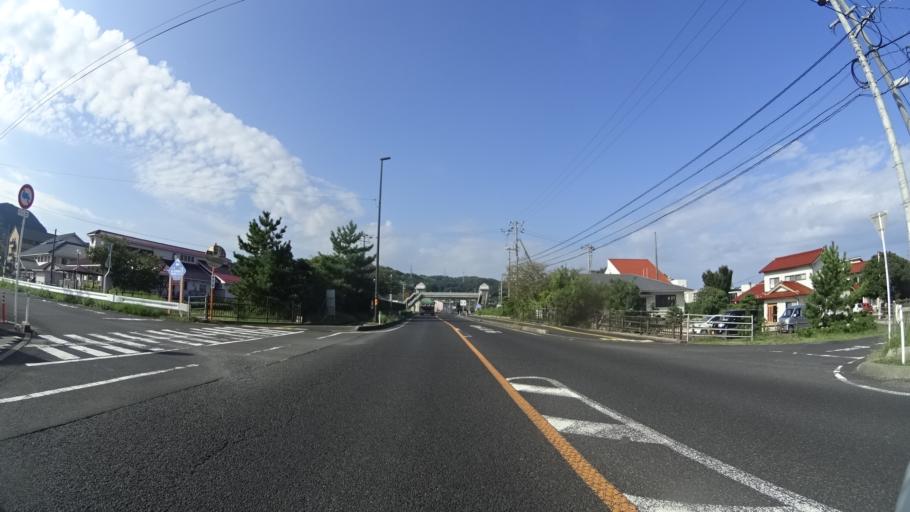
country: JP
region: Shimane
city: Odacho-oda
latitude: 35.2857
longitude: 132.6270
